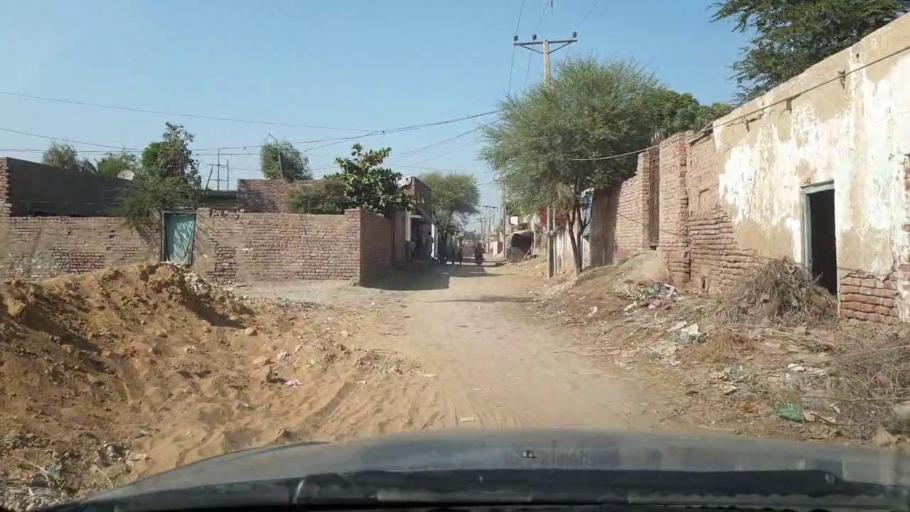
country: PK
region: Sindh
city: Tando Muhammad Khan
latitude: 25.1315
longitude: 68.5486
